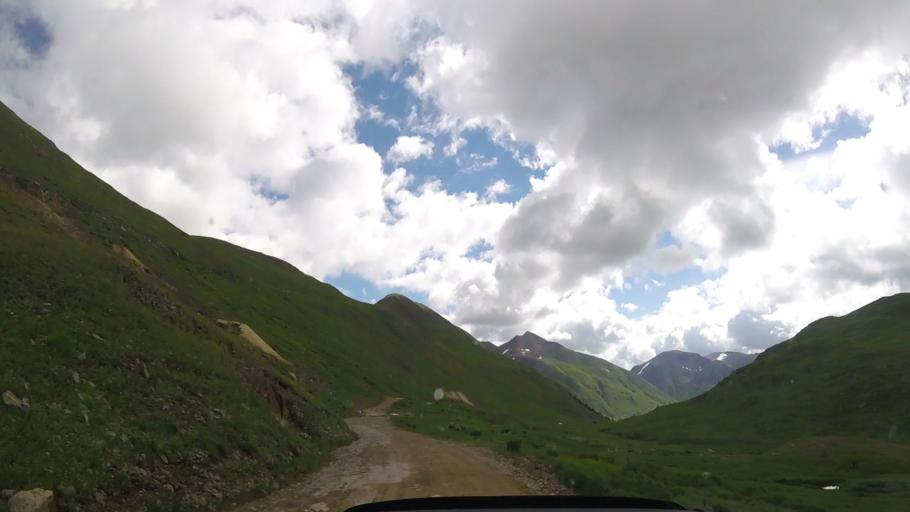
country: US
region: Colorado
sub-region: Ouray County
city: Ouray
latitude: 37.9310
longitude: -107.6030
